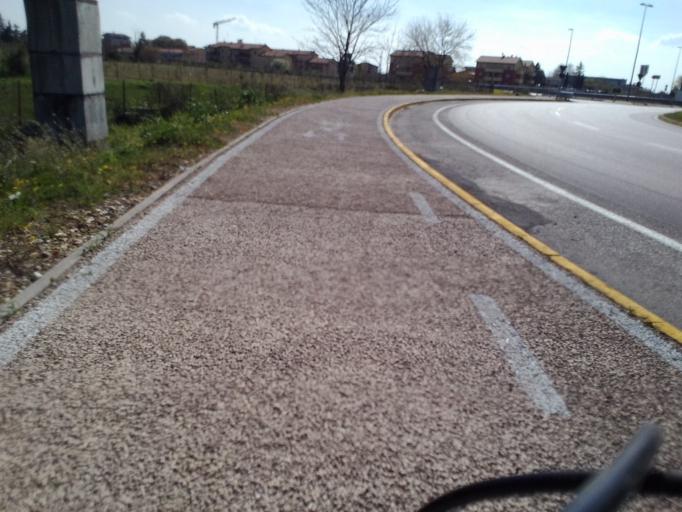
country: IT
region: Veneto
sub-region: Provincia di Verona
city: Dossobuono
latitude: 45.4104
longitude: 10.9286
